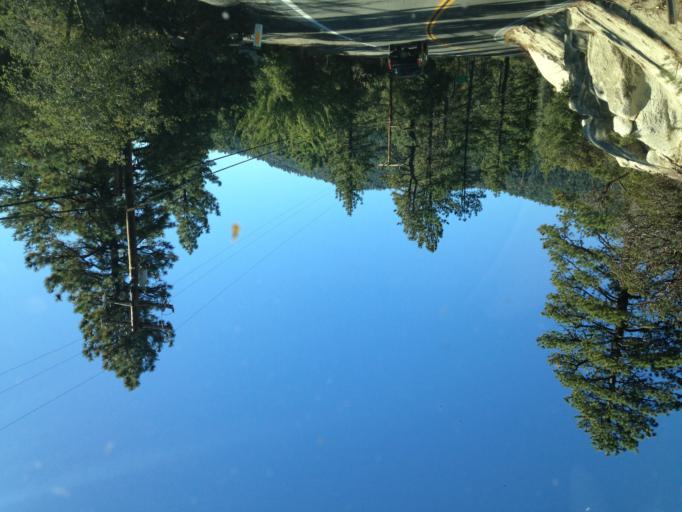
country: US
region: California
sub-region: Riverside County
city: Idyllwild
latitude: 33.7508
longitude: -116.7168
